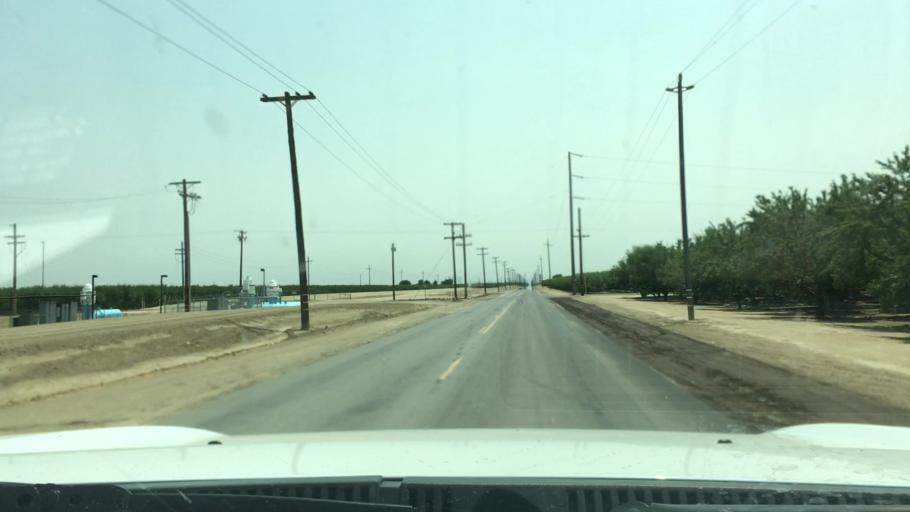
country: US
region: California
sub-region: Kern County
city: Wasco
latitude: 35.6170
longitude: -119.4379
